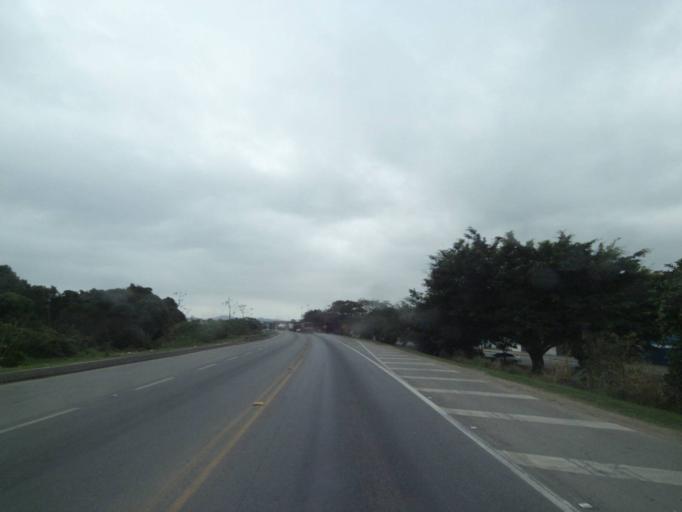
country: BR
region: Parana
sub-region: Paranagua
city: Paranagua
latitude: -25.5321
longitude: -48.5500
